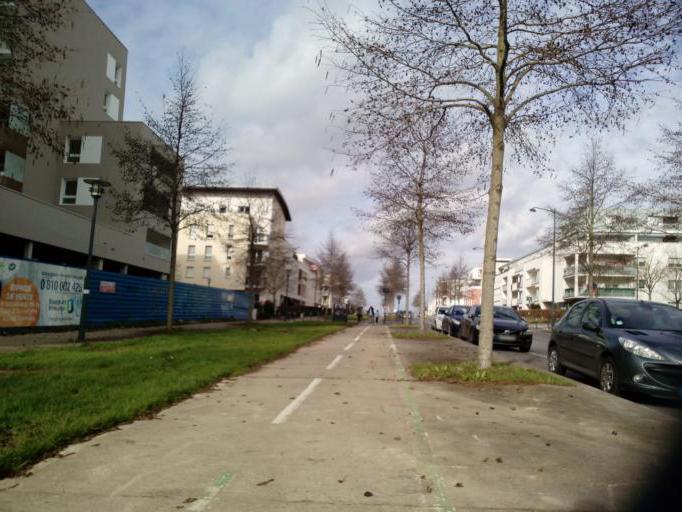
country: FR
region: Brittany
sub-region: Departement d'Ille-et-Vilaine
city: Saint-Gregoire
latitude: 48.1283
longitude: -1.7033
